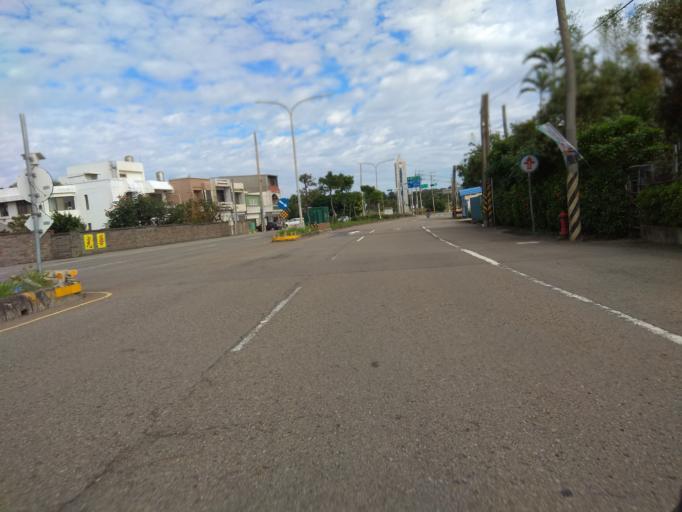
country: TW
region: Taiwan
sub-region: Hsinchu
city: Zhubei
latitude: 25.0326
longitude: 121.0715
